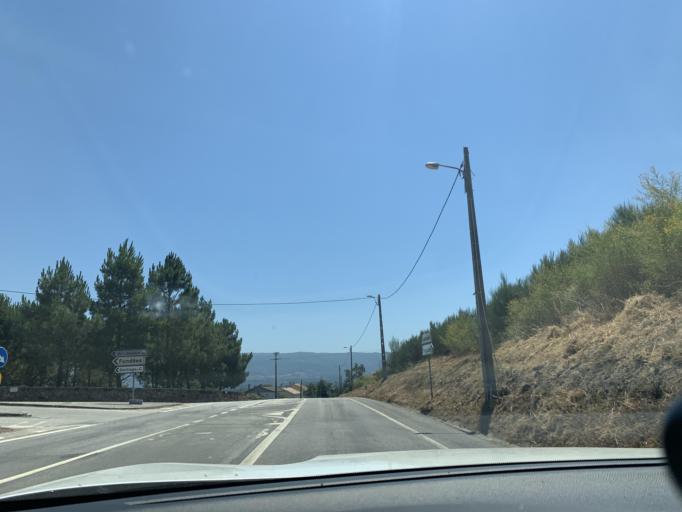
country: PT
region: Viseu
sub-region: Mangualde
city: Mangualde
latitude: 40.5711
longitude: -7.7257
